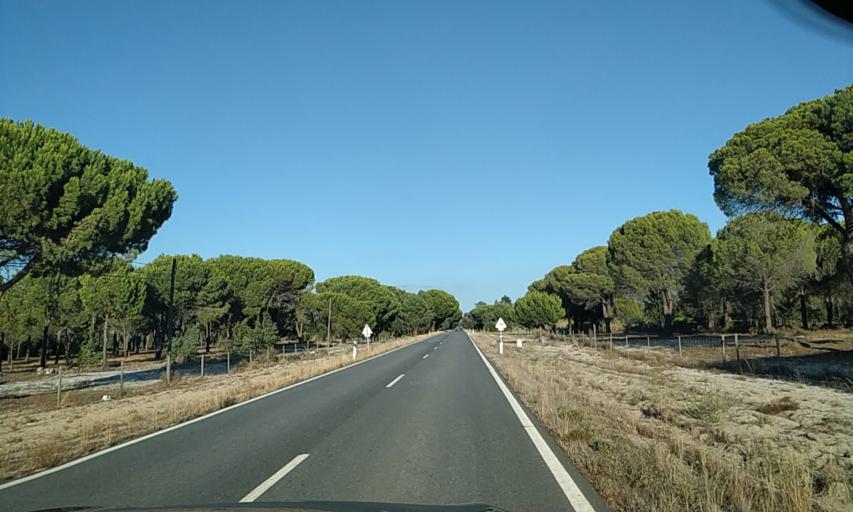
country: PT
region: Setubal
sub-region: Alcacer do Sal
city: Alcacer do Sal
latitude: 38.3940
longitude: -8.6559
